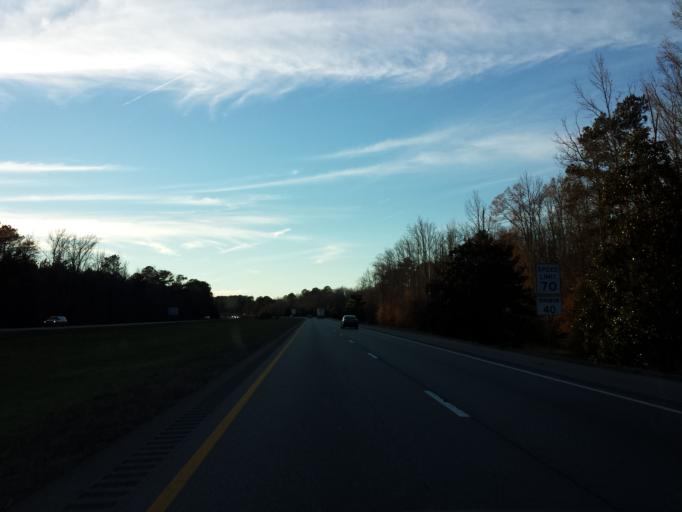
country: US
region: Mississippi
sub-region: Lauderdale County
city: Marion
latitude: 32.4137
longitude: -88.5162
